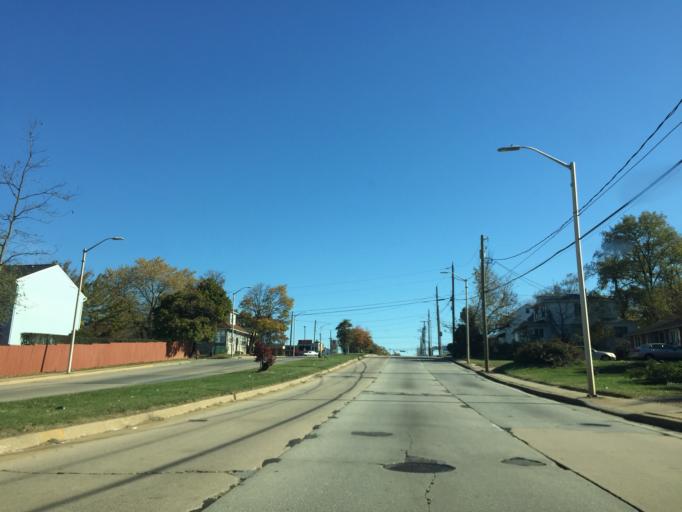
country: US
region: Maryland
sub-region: Baltimore County
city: Lansdowne
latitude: 39.2519
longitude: -76.6497
